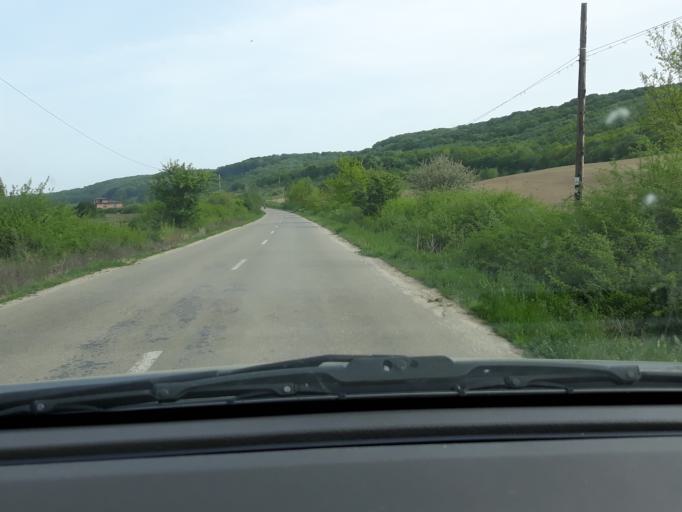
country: RO
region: Bihor
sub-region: Comuna Sanmartin
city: Sanmartin
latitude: 46.9811
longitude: 22.0008
